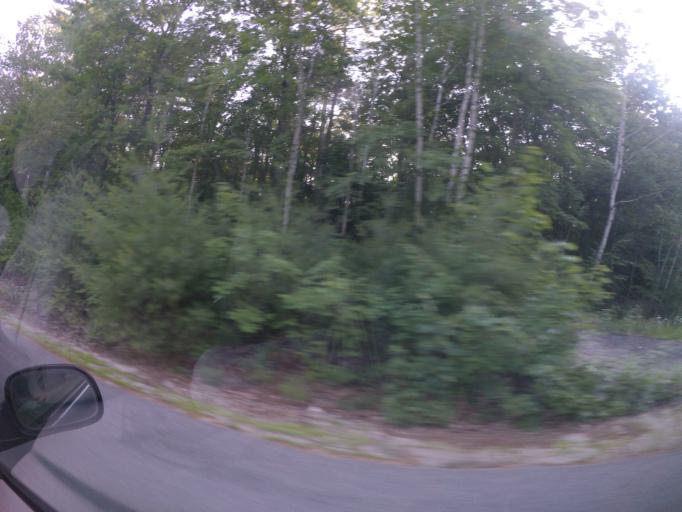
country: US
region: Maine
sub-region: Cumberland County
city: Raymond
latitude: 43.8904
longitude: -70.4164
